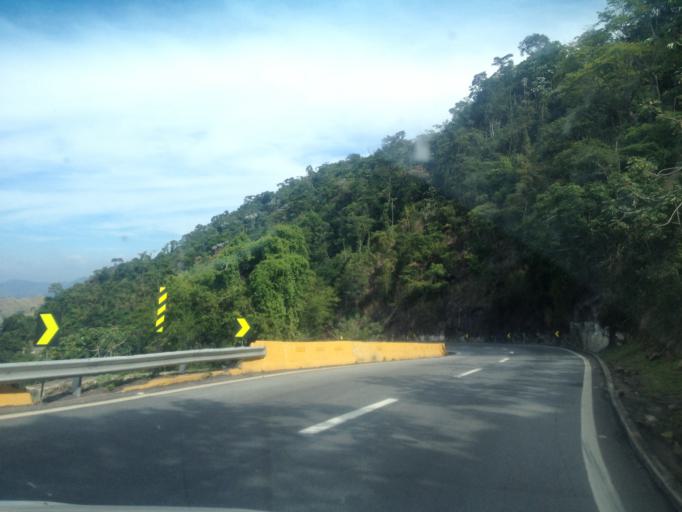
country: BR
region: Rio de Janeiro
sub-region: Pirai
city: Pirai
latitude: -22.6696
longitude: -43.8268
